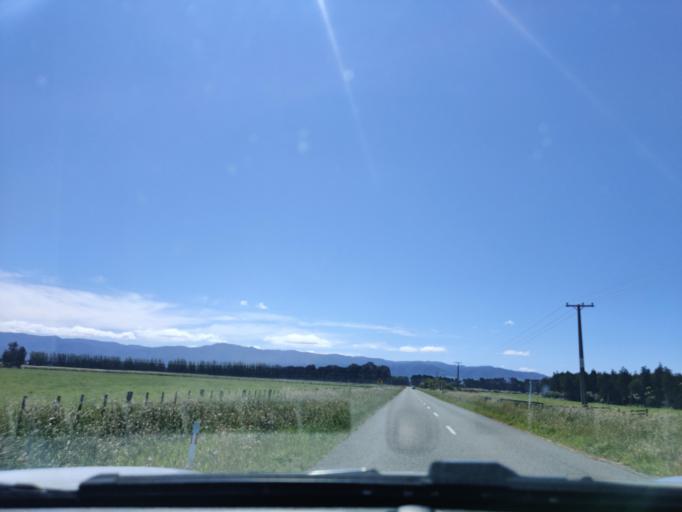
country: NZ
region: Wellington
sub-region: Upper Hutt City
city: Upper Hutt
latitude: -41.2852
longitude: 175.2690
